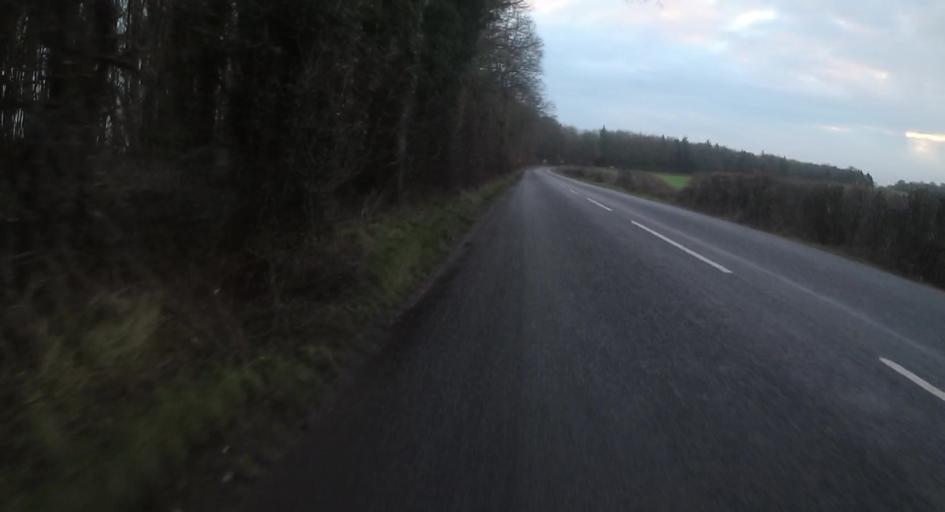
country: GB
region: England
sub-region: Hampshire
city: Overton
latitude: 51.2820
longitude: -1.2832
